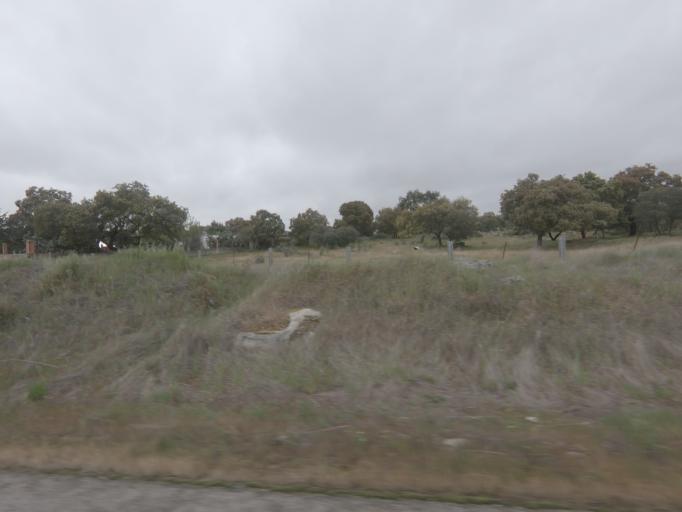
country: ES
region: Extremadura
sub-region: Provincia de Caceres
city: Caceres
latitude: 39.3992
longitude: -6.4221
